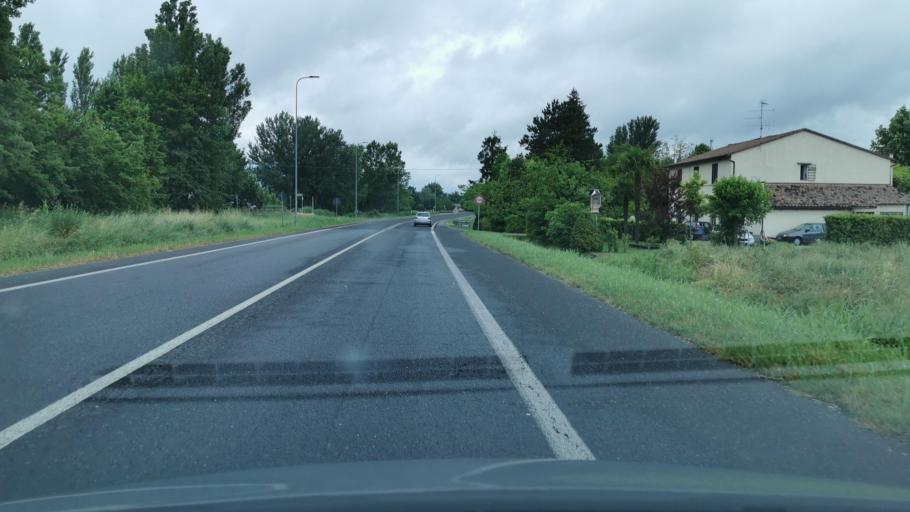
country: IT
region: Emilia-Romagna
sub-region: Provincia di Ravenna
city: Cotignola
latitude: 44.3724
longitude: 11.9442
